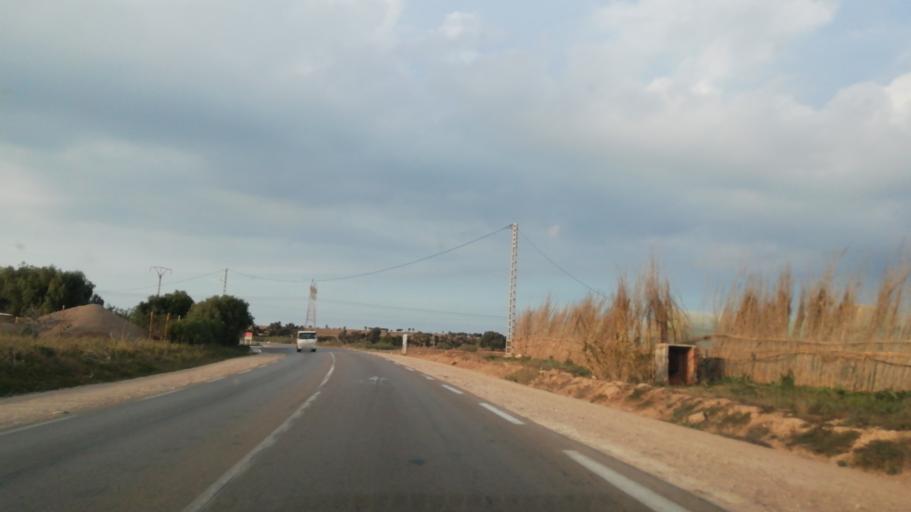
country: DZ
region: Oran
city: Ain el Bya
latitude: 35.7793
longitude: -0.0974
